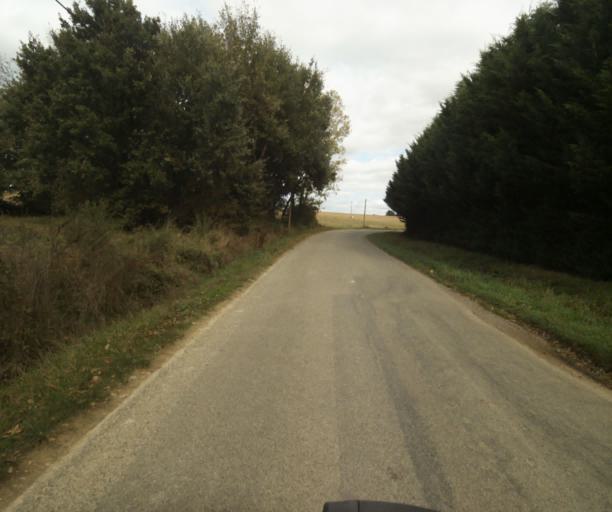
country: FR
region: Midi-Pyrenees
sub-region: Departement du Tarn-et-Garonne
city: Verdun-sur-Garonne
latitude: 43.8577
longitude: 1.1277
